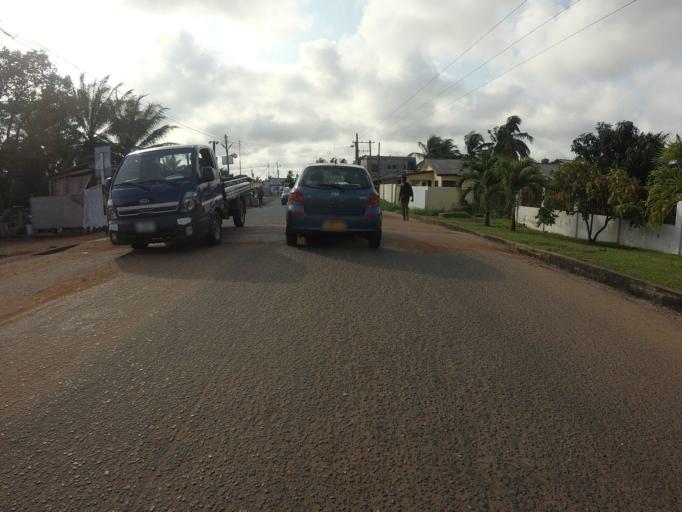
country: GH
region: Greater Accra
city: Nungua
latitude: 5.6172
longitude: -0.0782
